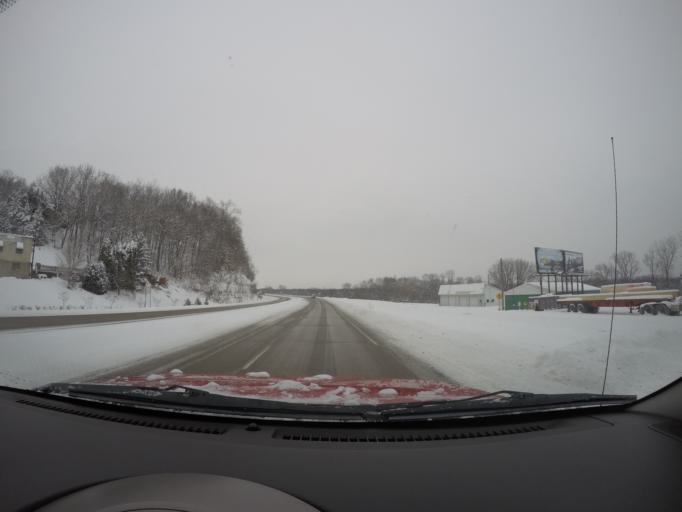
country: US
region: Minnesota
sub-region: Houston County
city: La Crescent
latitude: 43.8347
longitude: -91.3003
